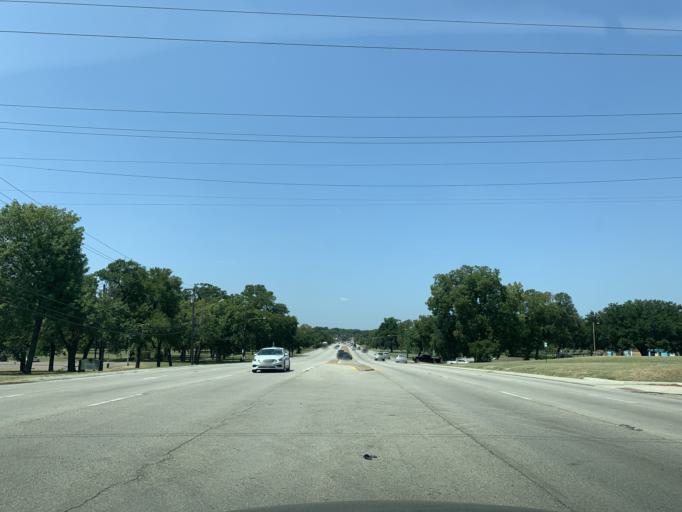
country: US
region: Texas
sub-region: Dallas County
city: Hutchins
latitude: 32.6847
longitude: -96.7955
